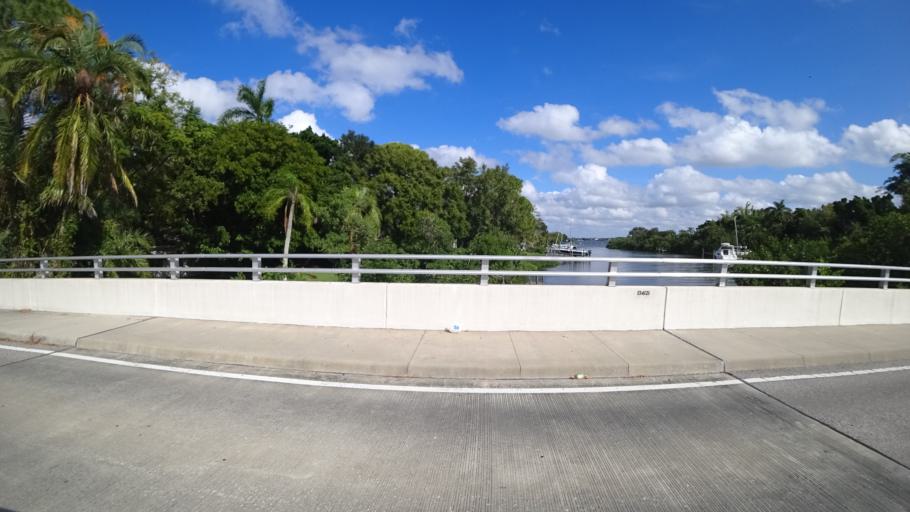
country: US
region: Florida
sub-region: Manatee County
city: West Bradenton
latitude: 27.5011
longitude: -82.5998
